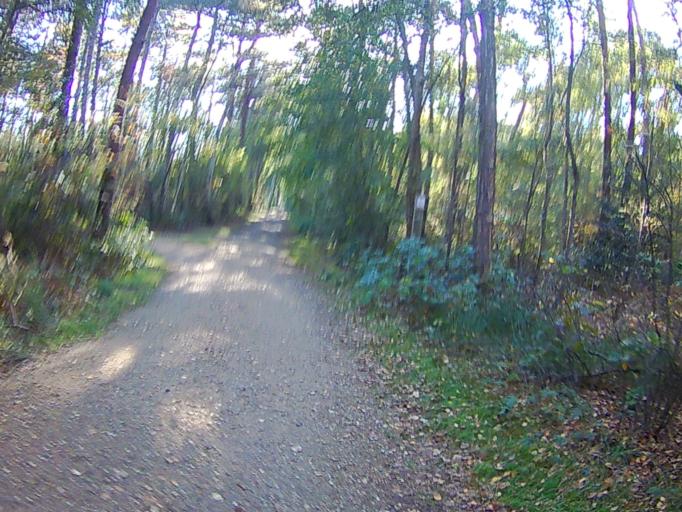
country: BE
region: Flanders
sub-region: Provincie Antwerpen
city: Stabroek
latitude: 51.3376
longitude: 4.3925
